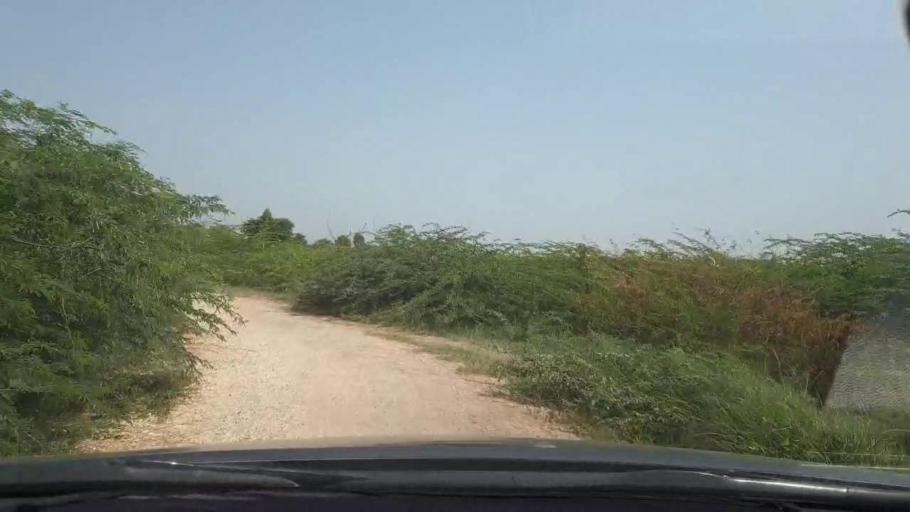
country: PK
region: Sindh
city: Tando Bago
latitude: 24.7792
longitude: 69.1903
